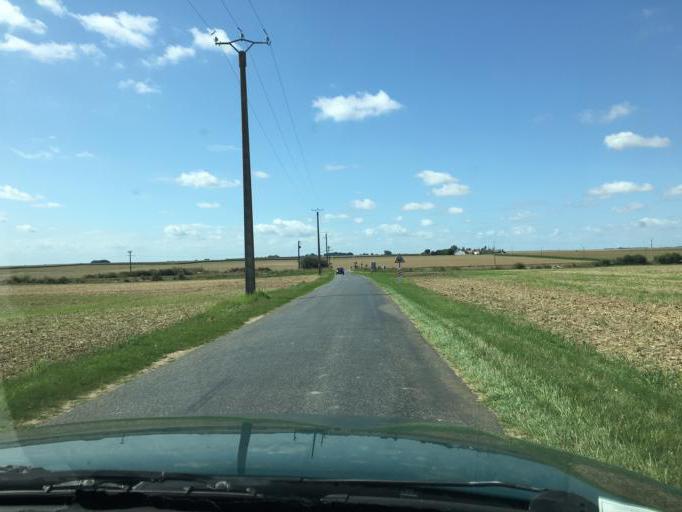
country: FR
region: Centre
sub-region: Departement du Loiret
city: Patay
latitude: 48.0214
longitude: 1.7302
